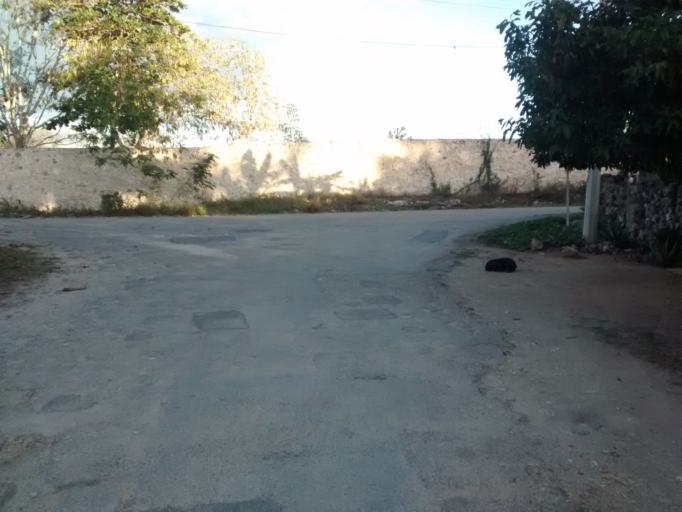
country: MX
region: Yucatan
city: Valladolid
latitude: 20.6846
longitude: -88.1877
